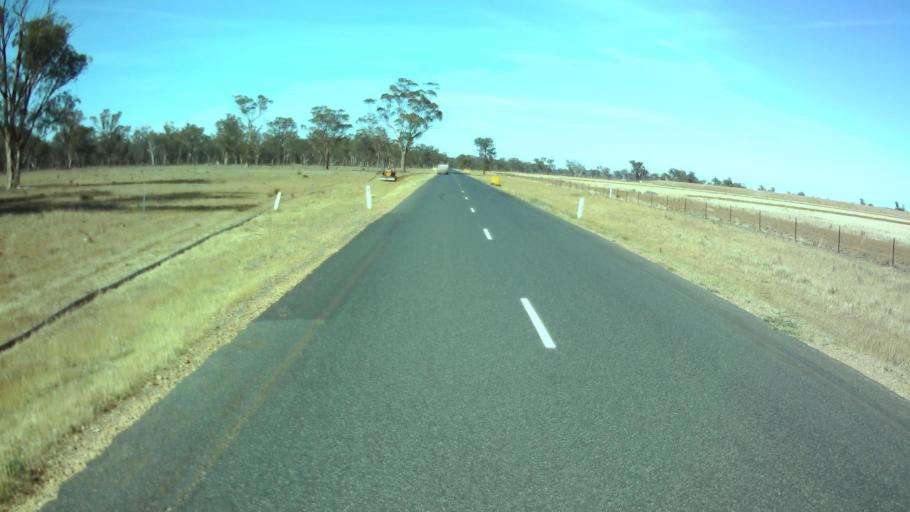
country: AU
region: New South Wales
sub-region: Weddin
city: Grenfell
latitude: -34.1269
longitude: 147.8018
